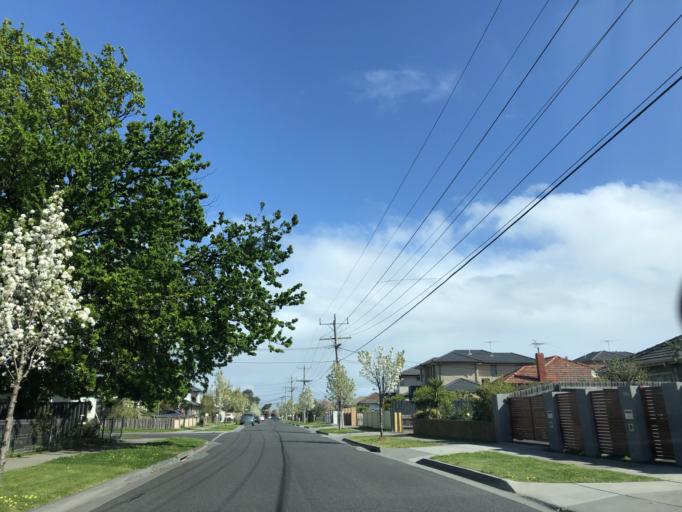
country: AU
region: Victoria
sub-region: Kingston
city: Clayton South
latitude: -37.9296
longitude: 145.1163
